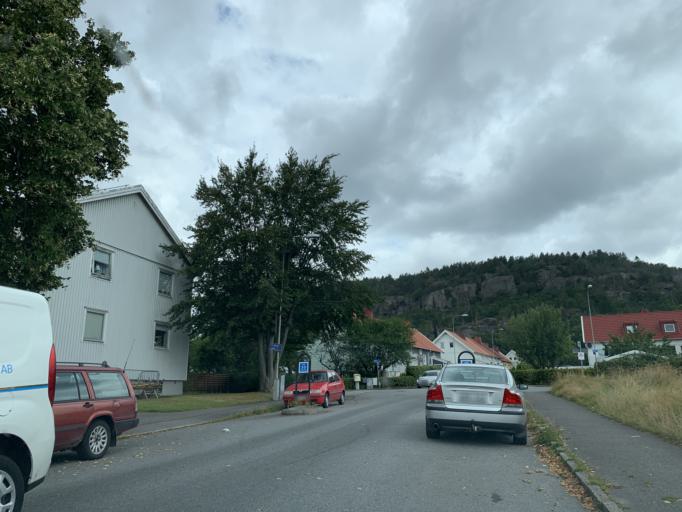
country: SE
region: Vaestra Goetaland
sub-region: Partille Kommun
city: Partille
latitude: 57.7397
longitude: 12.0698
